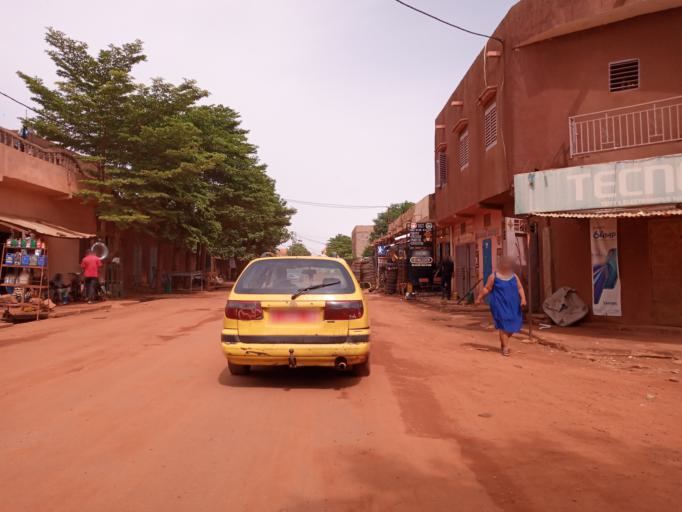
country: ML
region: Bamako
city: Bamako
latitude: 12.5534
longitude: -7.9971
